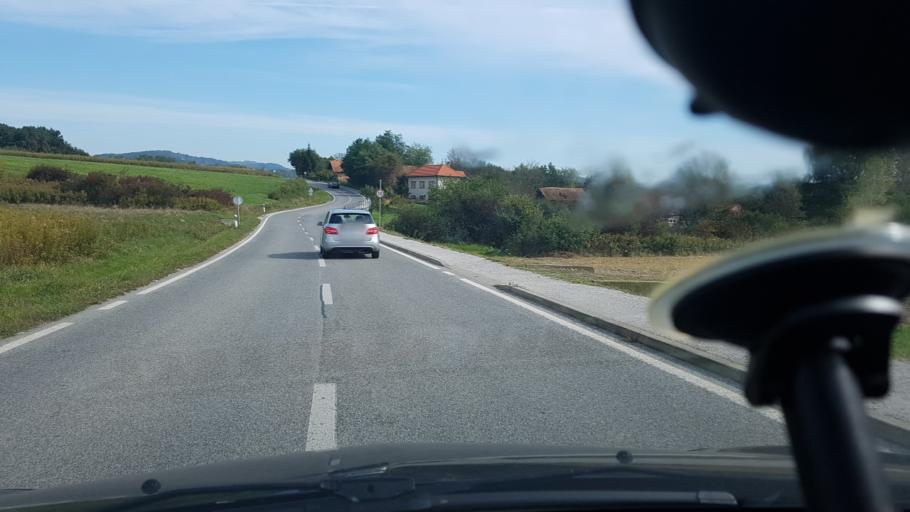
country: HR
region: Krapinsko-Zagorska
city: Marija Bistrica
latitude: 46.0797
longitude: 16.1957
